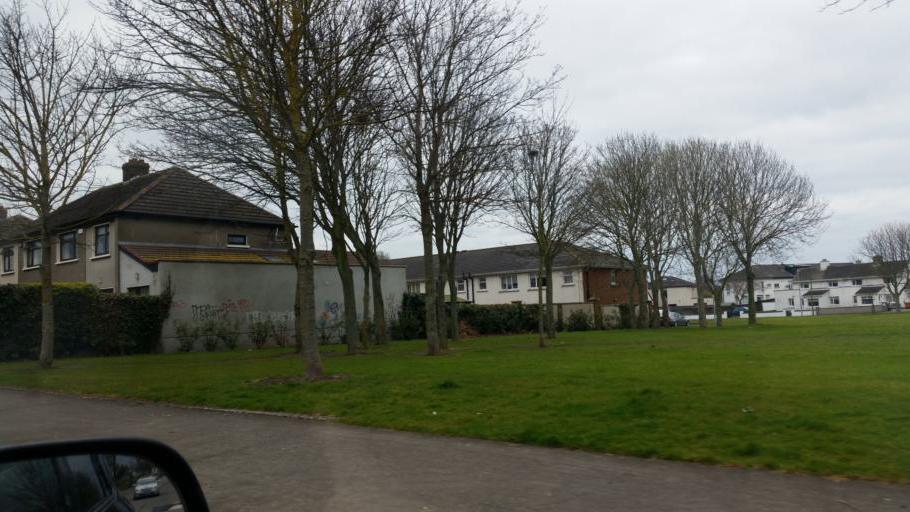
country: IE
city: Bayside
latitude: 53.3960
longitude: -6.1426
